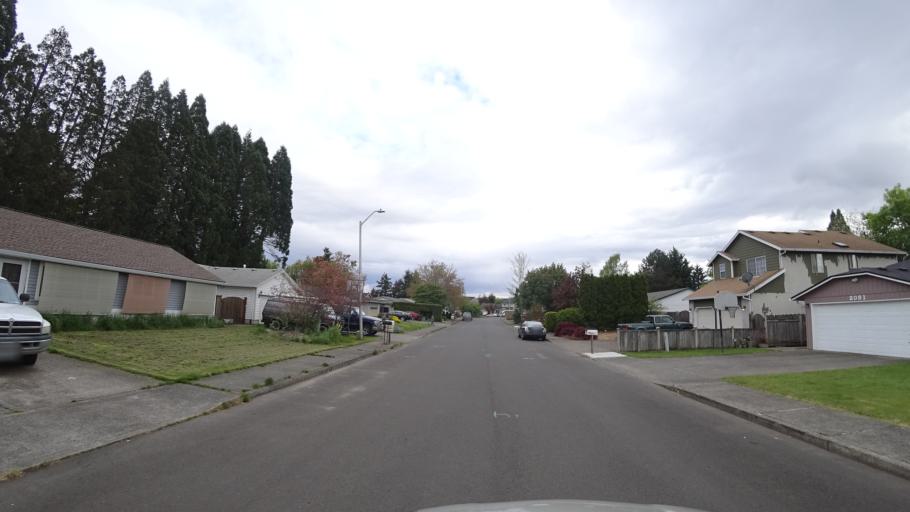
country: US
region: Oregon
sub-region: Washington County
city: Hillsboro
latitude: 45.5401
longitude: -122.9683
